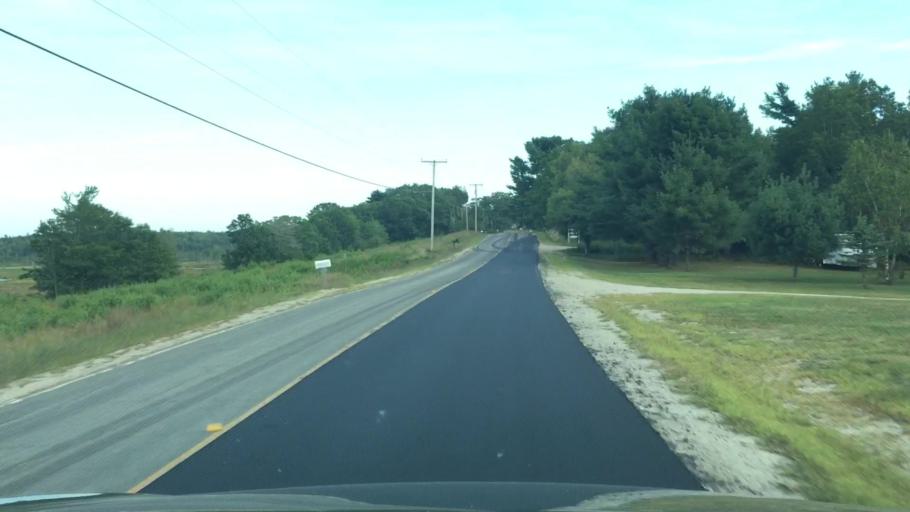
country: US
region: Maine
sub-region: Hancock County
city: Surry
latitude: 44.5151
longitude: -68.6032
